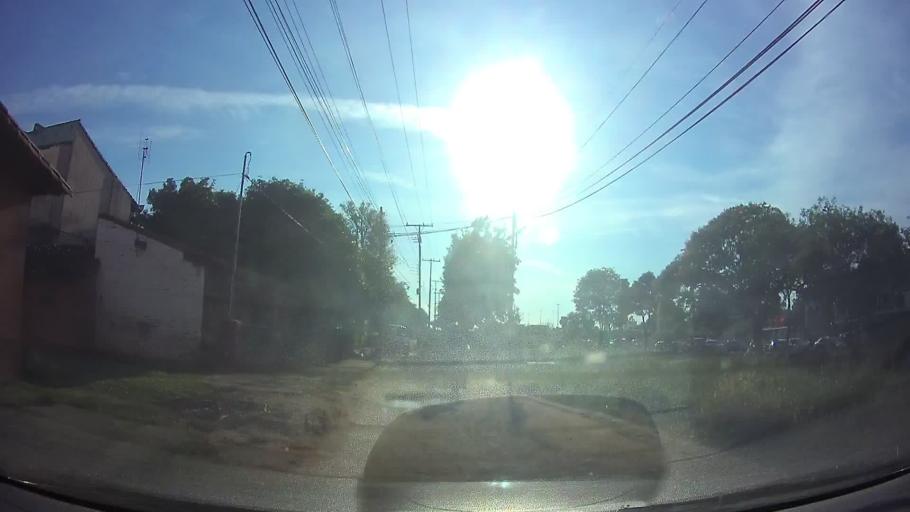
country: PY
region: Central
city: Fernando de la Mora
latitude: -25.2638
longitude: -57.5090
